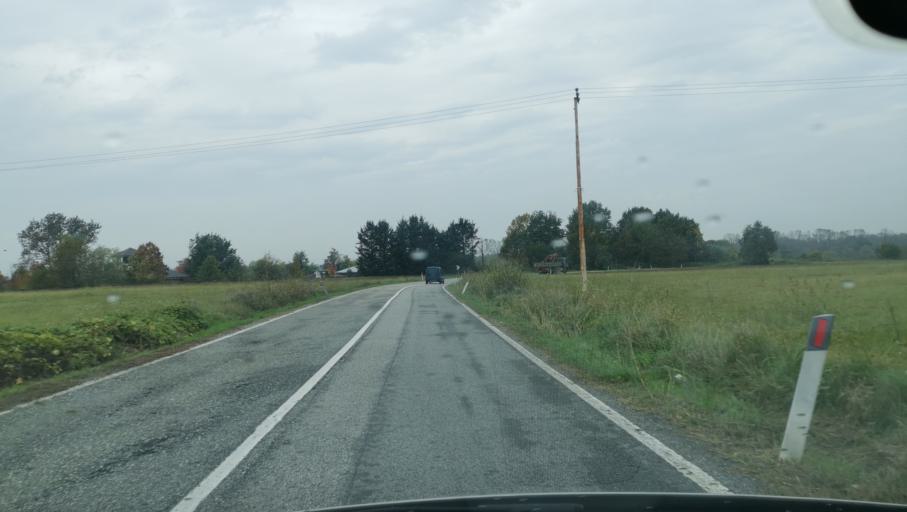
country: IT
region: Piedmont
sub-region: Provincia di Torino
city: Castiglione Torinese
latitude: 45.1252
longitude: 7.8167
